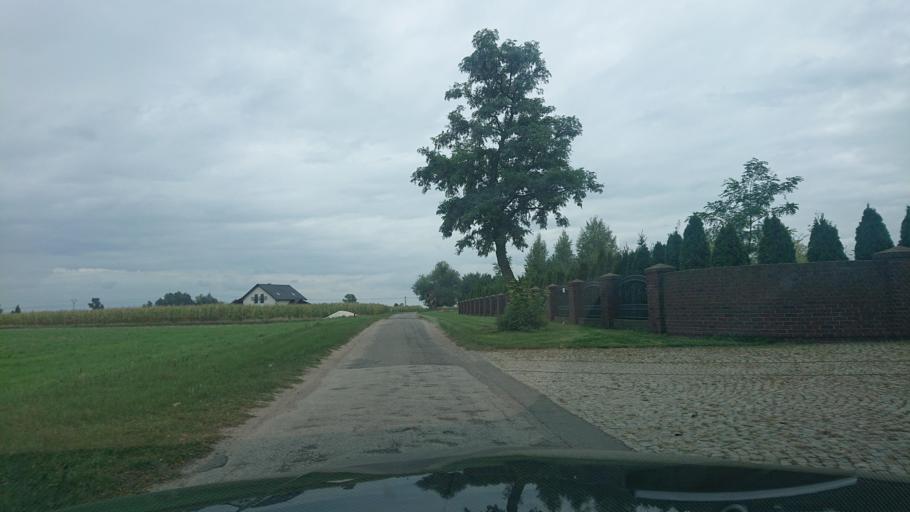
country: PL
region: Greater Poland Voivodeship
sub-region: Powiat gnieznienski
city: Niechanowo
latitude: 52.4797
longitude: 17.6189
